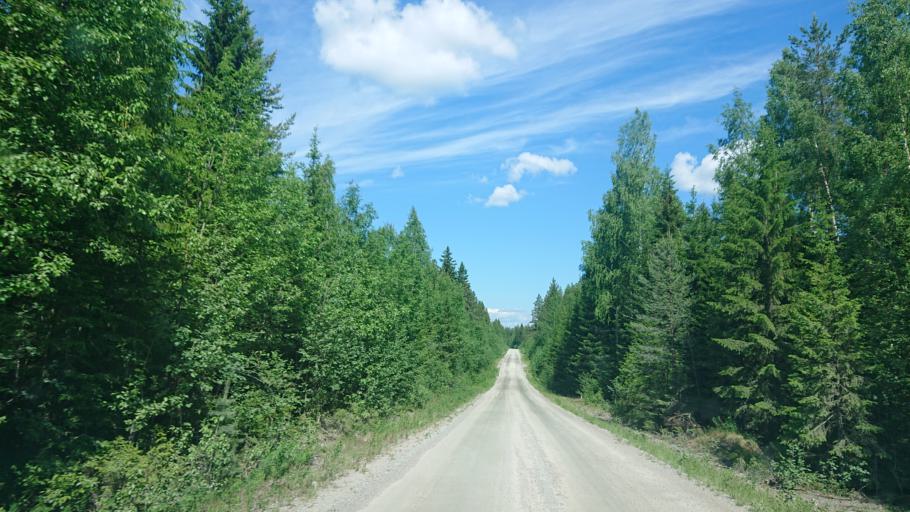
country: SE
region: Vaesternorrland
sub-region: Solleftea Kommun
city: Solleftea
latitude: 62.9475
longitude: 17.1353
